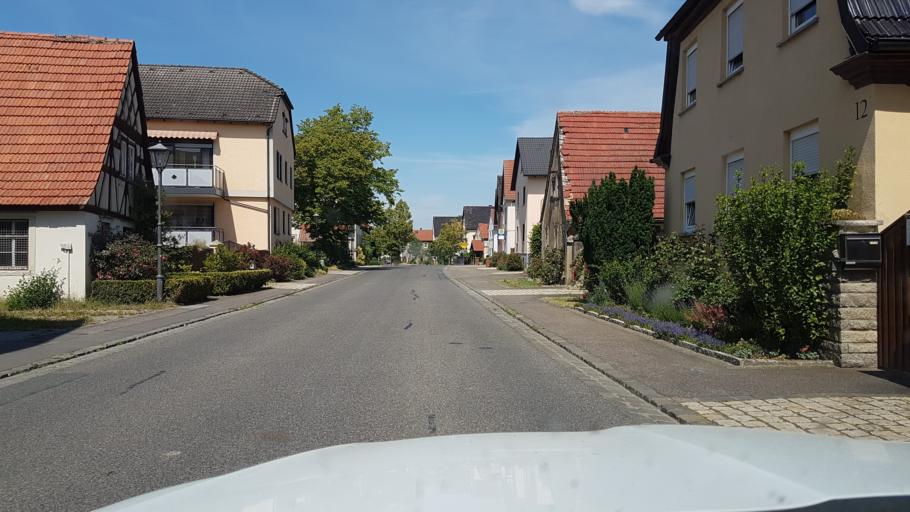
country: DE
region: Bavaria
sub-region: Regierungsbezirk Unterfranken
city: Hassfurt
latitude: 49.9971
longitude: 10.5025
